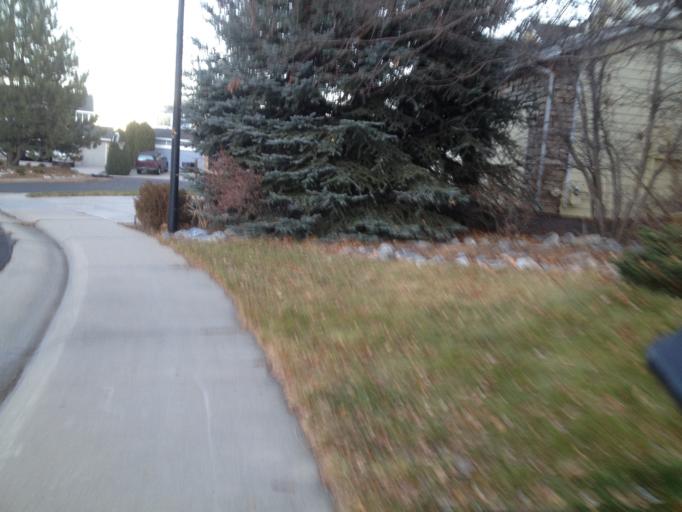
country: US
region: Colorado
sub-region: Boulder County
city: Superior
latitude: 39.9572
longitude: -105.1478
